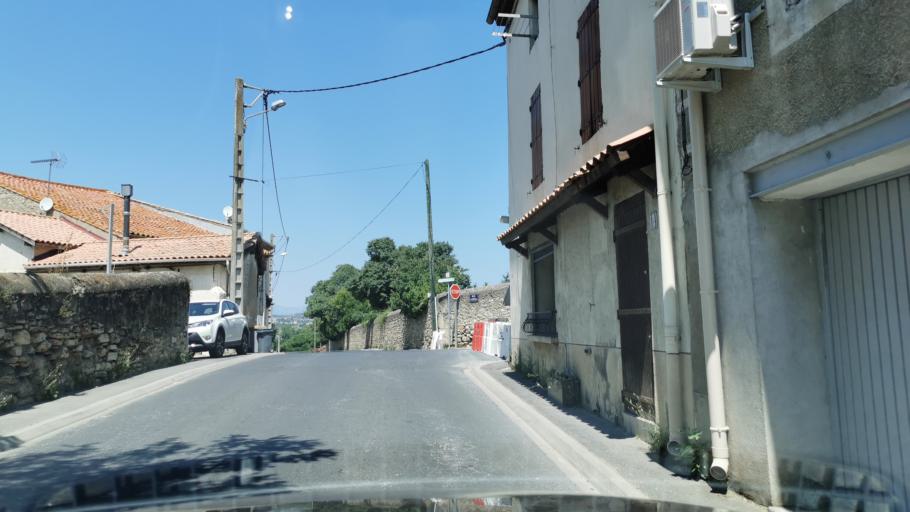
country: FR
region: Languedoc-Roussillon
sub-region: Departement de l'Herault
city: Maureilhan
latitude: 43.3590
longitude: 3.1192
